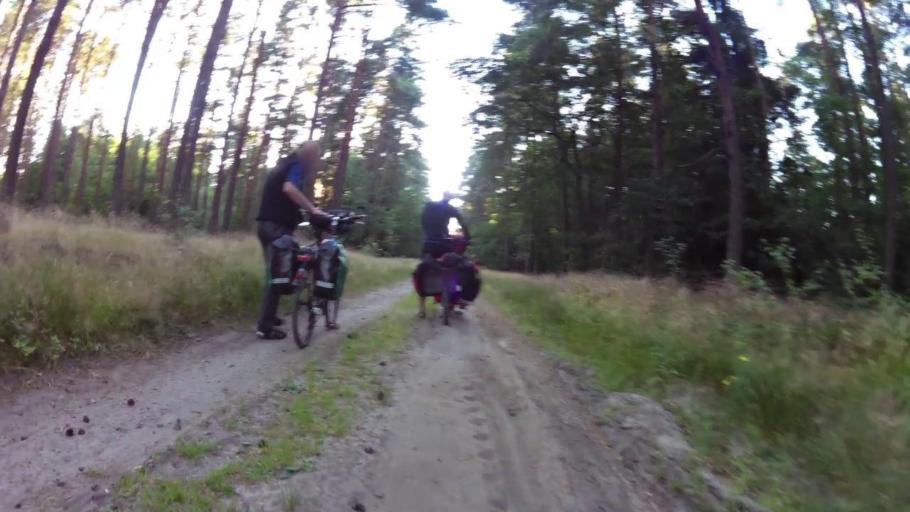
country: PL
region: West Pomeranian Voivodeship
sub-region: Powiat lobeski
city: Lobez
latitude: 53.7427
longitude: 15.6509
